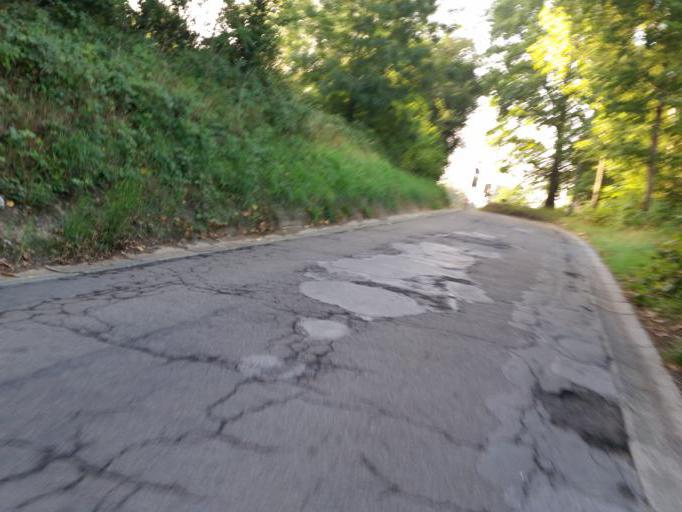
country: BE
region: Flanders
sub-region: Provincie Vlaams-Brabant
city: Grimbergen
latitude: 50.9013
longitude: 4.3843
